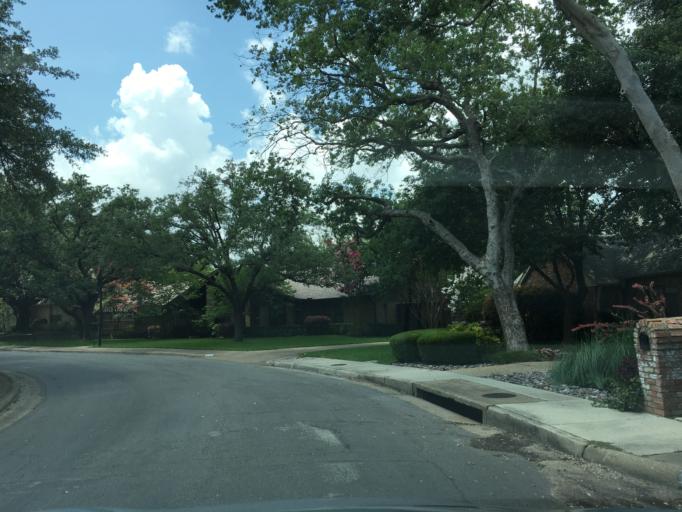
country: US
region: Texas
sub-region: Dallas County
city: University Park
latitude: 32.8937
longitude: -96.7848
